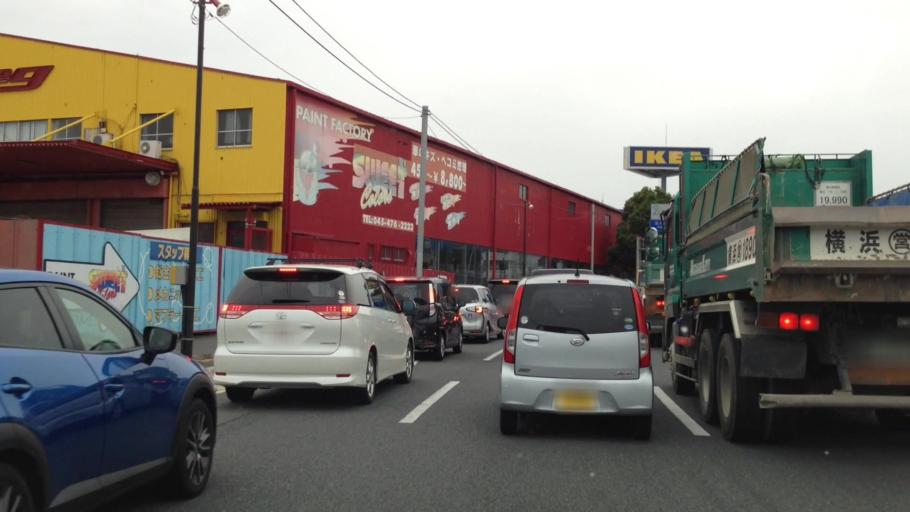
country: JP
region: Kanagawa
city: Yokohama
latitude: 35.5193
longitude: 139.5910
